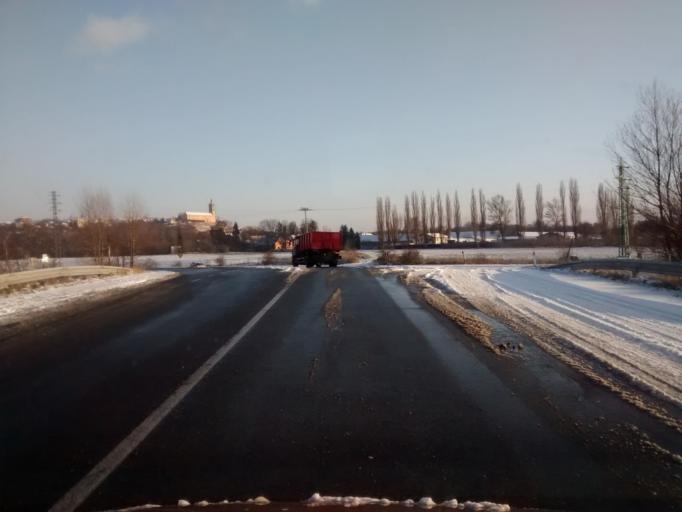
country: CZ
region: Central Bohemia
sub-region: Okres Melnik
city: Melnik
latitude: 50.3562
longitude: 14.4543
